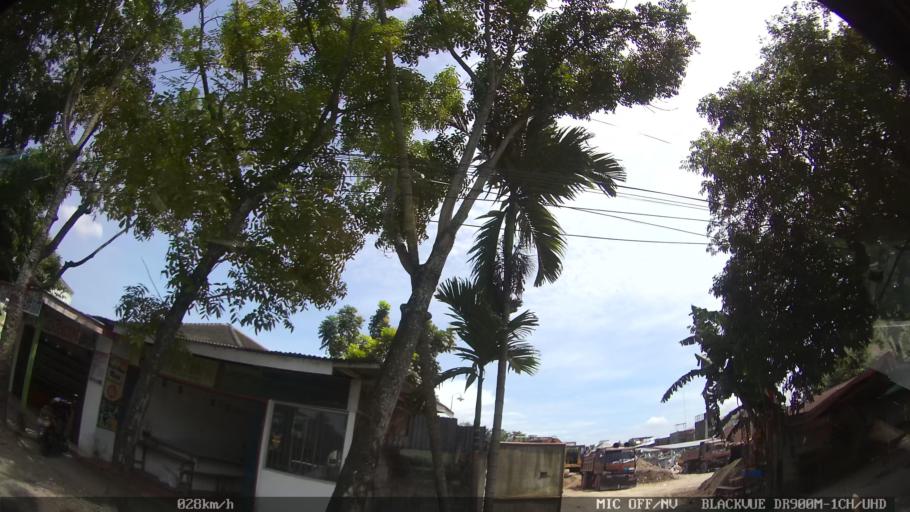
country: ID
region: North Sumatra
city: Sunggal
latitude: 3.5790
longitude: 98.6298
